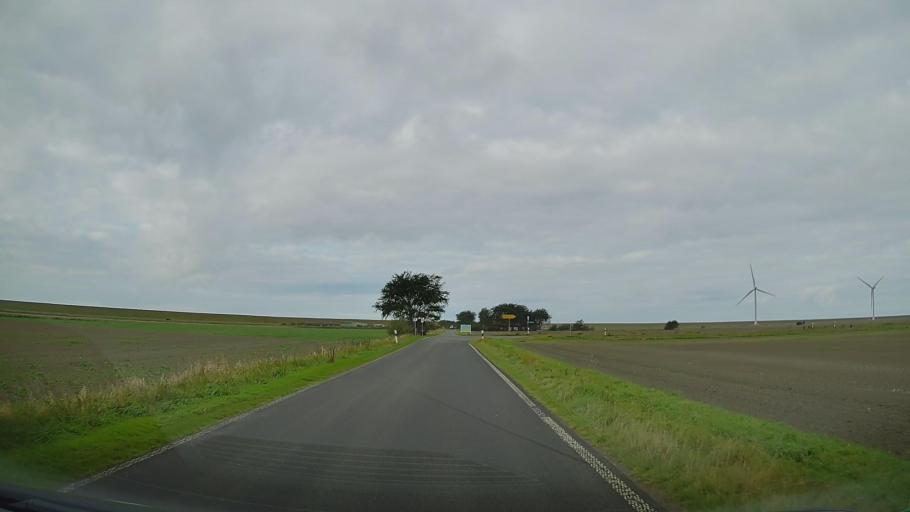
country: DE
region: Schleswig-Holstein
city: Friedrich-Wilhelm-Lubke-Koog
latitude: 54.8382
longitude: 8.6223
